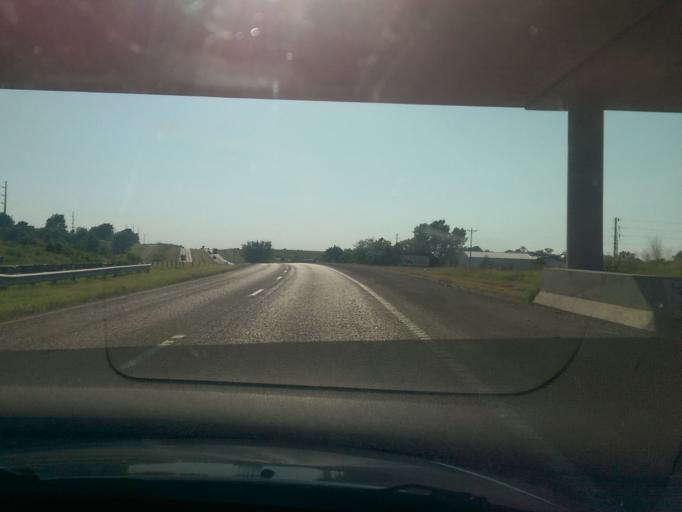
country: US
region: Missouri
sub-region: Lafayette County
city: Concordia
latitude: 38.9943
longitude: -93.5939
